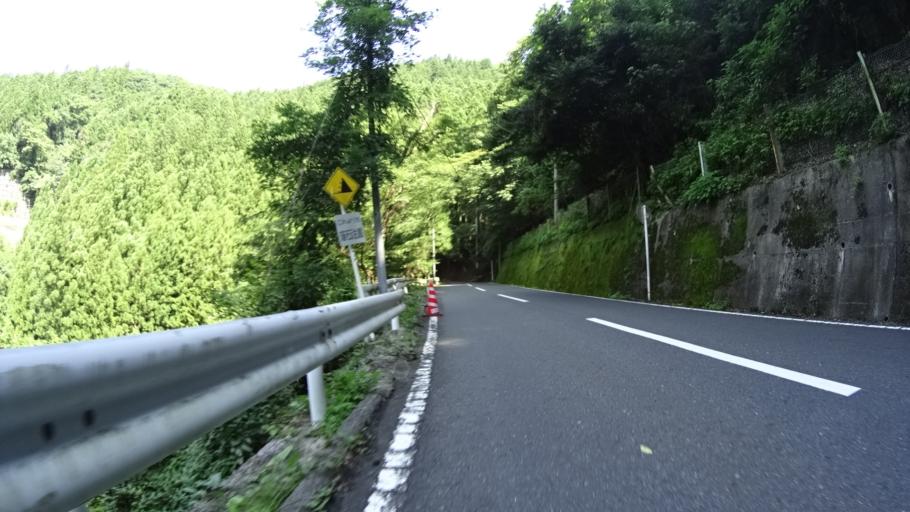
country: JP
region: Gunma
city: Tomioka
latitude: 36.0600
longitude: 138.8567
